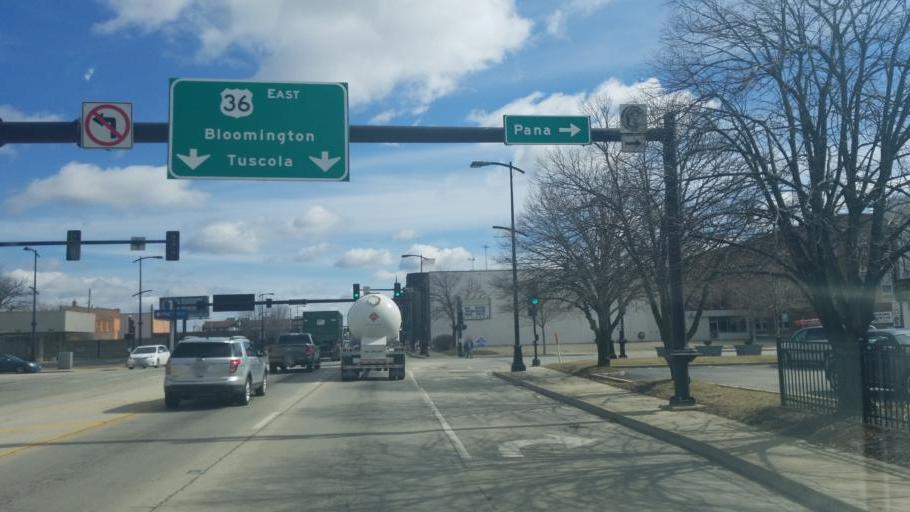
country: US
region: Illinois
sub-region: Macon County
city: Decatur
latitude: 39.8457
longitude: -88.9566
